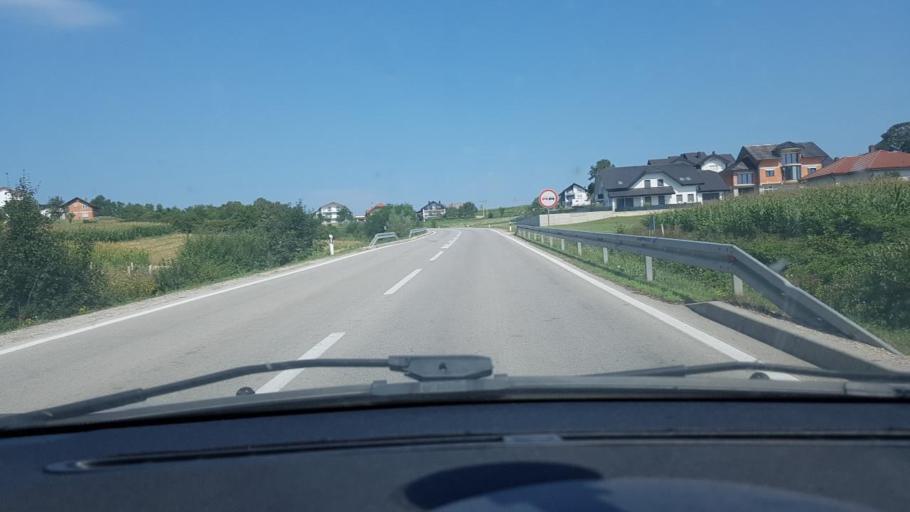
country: BA
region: Federation of Bosnia and Herzegovina
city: Velika Kladusa
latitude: 45.1955
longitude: 15.8092
